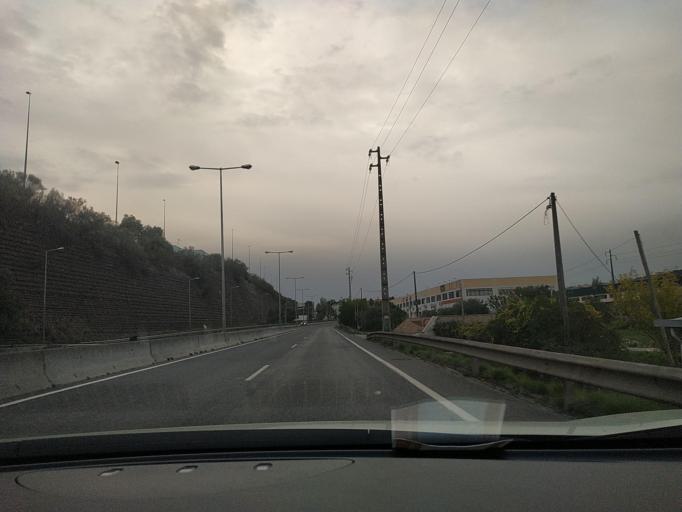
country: PT
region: Lisbon
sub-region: Loures
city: Santa Iria da Azoia
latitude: 38.8629
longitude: -9.1077
